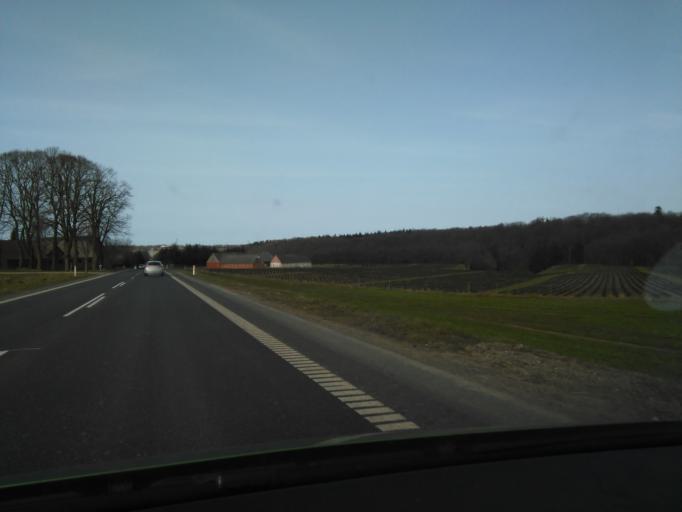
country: DK
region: Central Jutland
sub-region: Silkeborg Kommune
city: Kjellerup
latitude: 56.2372
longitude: 9.4734
